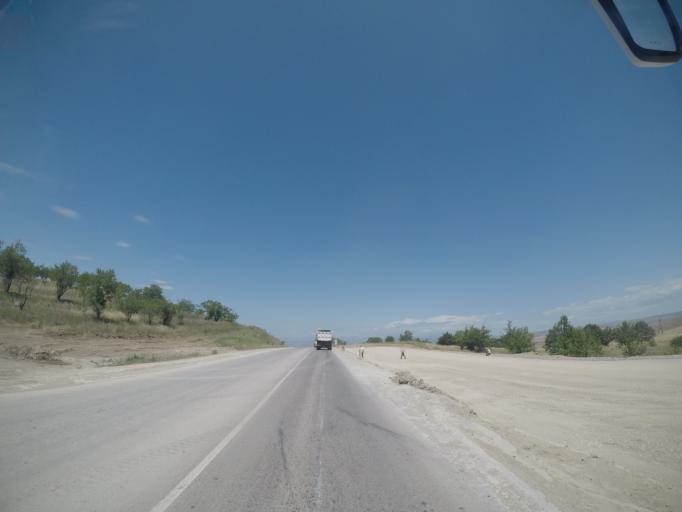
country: AZ
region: Qobustan
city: Qobustan
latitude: 40.5323
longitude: 48.7830
